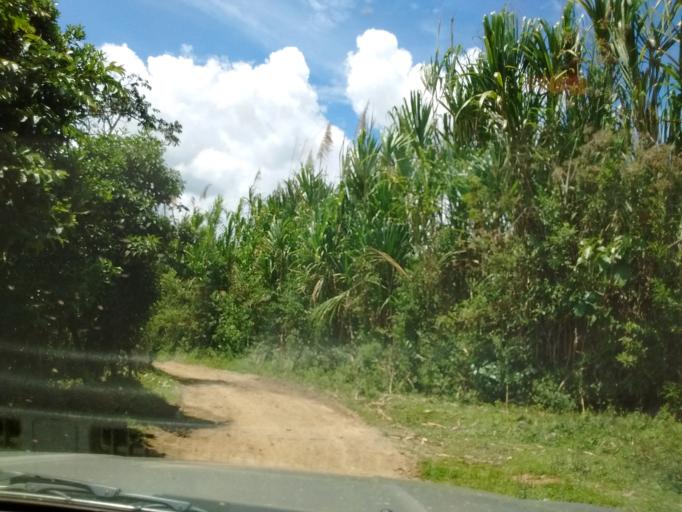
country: CO
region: Cauca
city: Villa Rica
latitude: 2.6570
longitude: -76.7675
